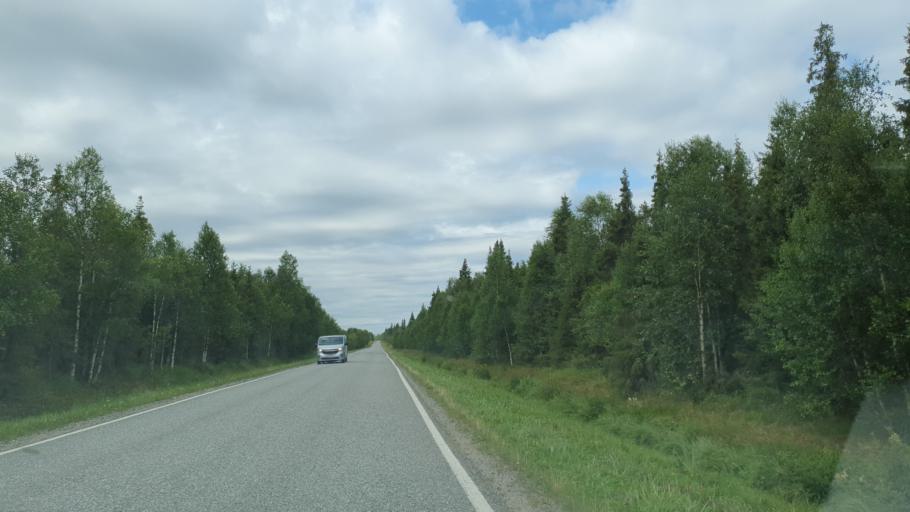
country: FI
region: Lapland
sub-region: Tunturi-Lappi
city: Kittilae
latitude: 67.6155
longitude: 25.3677
